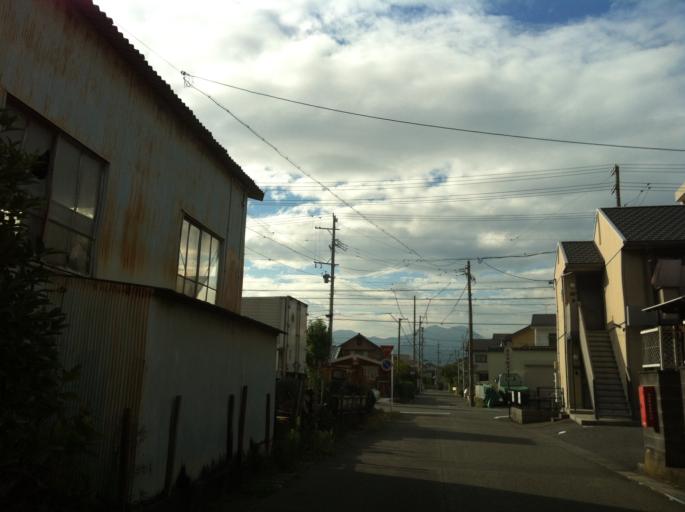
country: JP
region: Shizuoka
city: Shizuoka-shi
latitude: 35.0042
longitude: 138.4801
